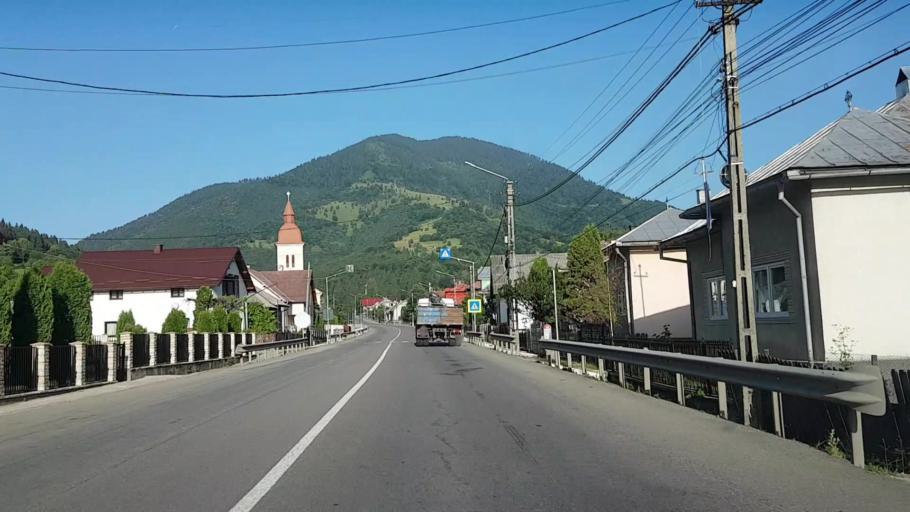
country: RO
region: Bistrita-Nasaud
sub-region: Comuna Tiha Bargaului
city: Tureac
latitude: 47.2104
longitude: 24.8577
